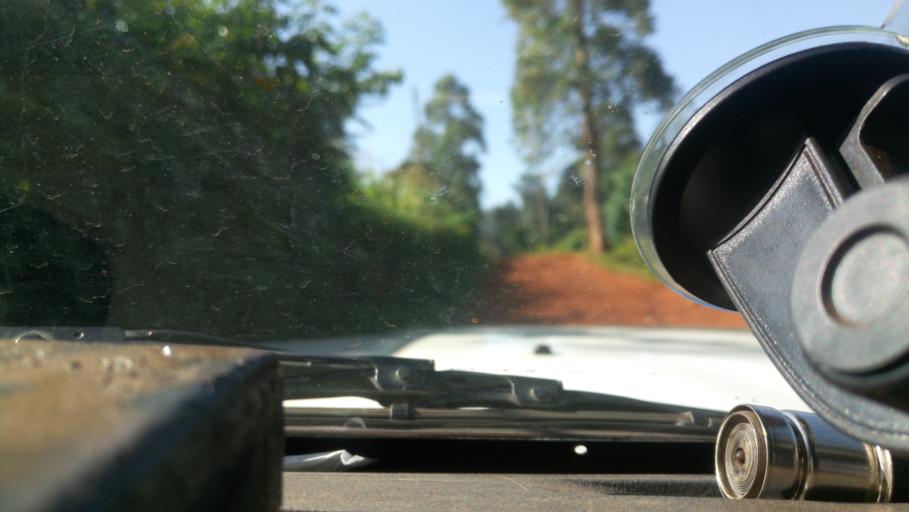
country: KE
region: Homa Bay
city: Oyugis
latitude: -0.5732
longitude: 34.7651
